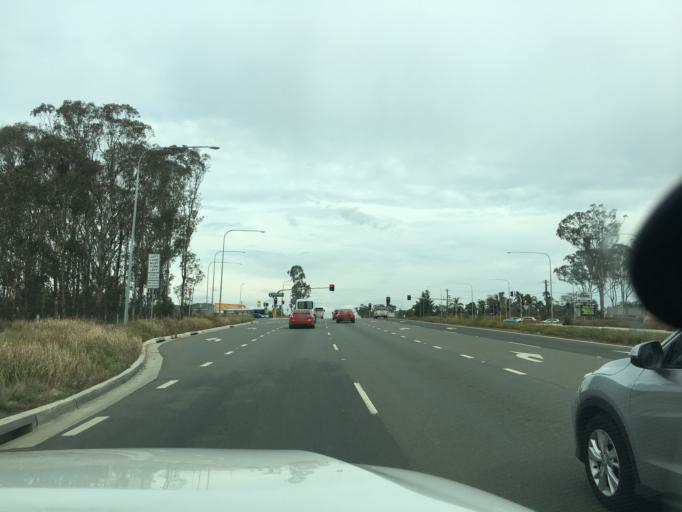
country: AU
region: New South Wales
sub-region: Campbelltown Municipality
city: Denham Court
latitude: -33.9675
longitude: 150.8153
